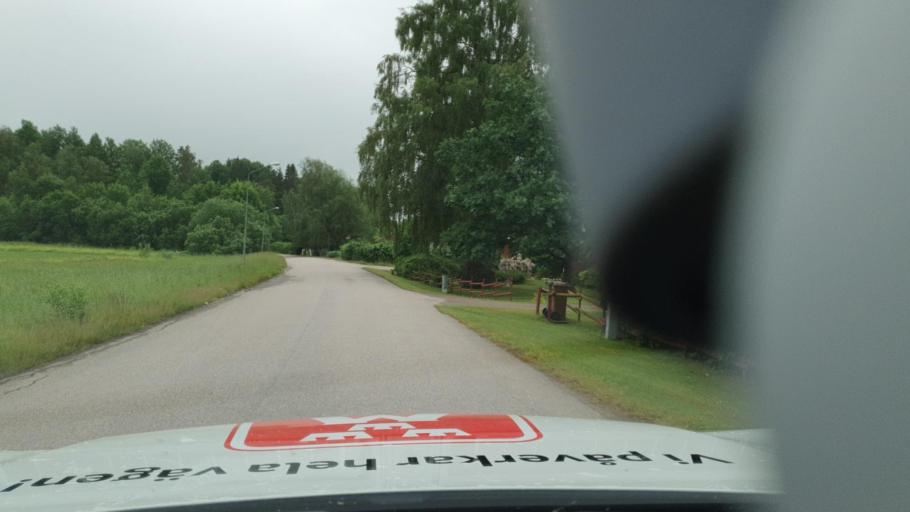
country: SE
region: Vaestra Goetaland
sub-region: Gullspangs Kommun
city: Gullspang
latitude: 59.0989
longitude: 14.1612
